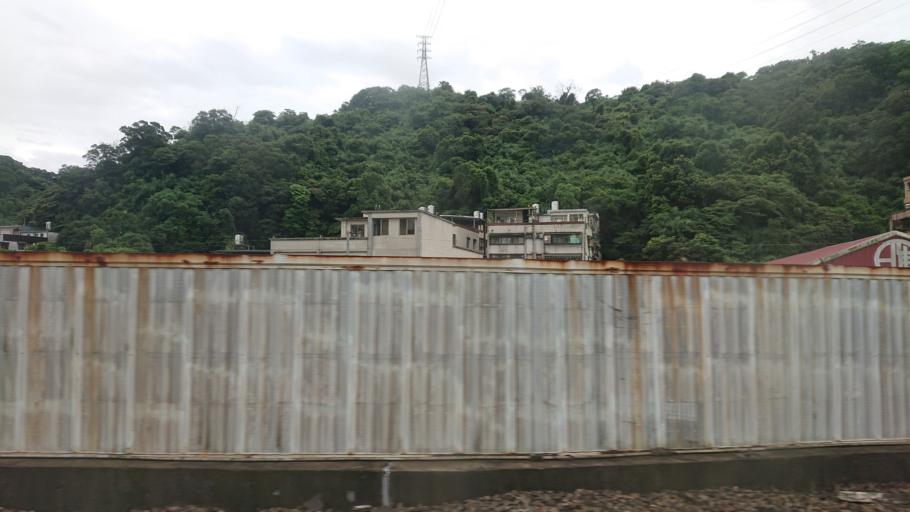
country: TW
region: Taiwan
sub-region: Keelung
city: Keelung
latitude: 25.1014
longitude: 121.7247
